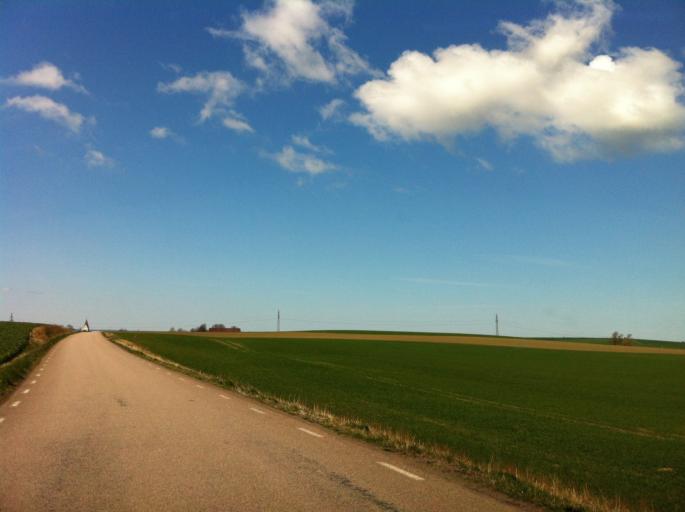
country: SE
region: Skane
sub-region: Landskrona
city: Asmundtorp
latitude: 55.9037
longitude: 12.9234
